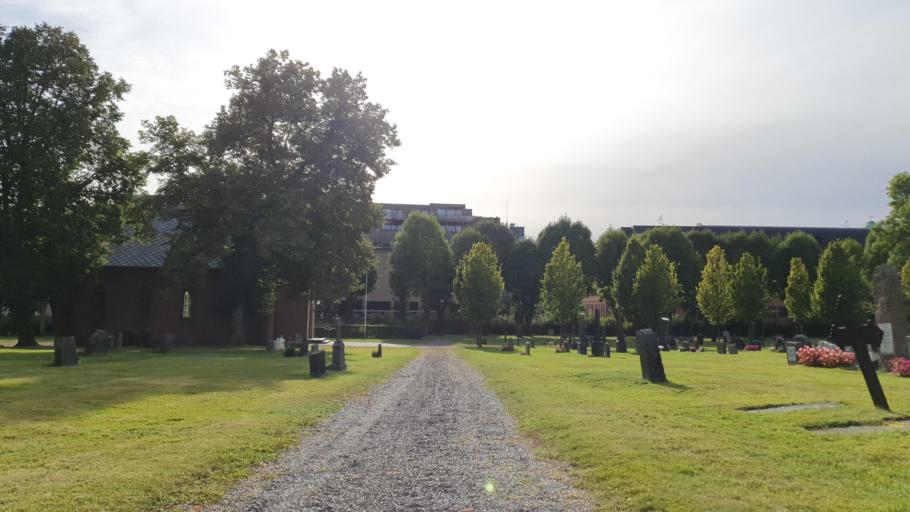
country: NO
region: Vestfold
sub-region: Tonsberg
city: Tonsberg
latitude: 59.2708
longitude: 10.4137
